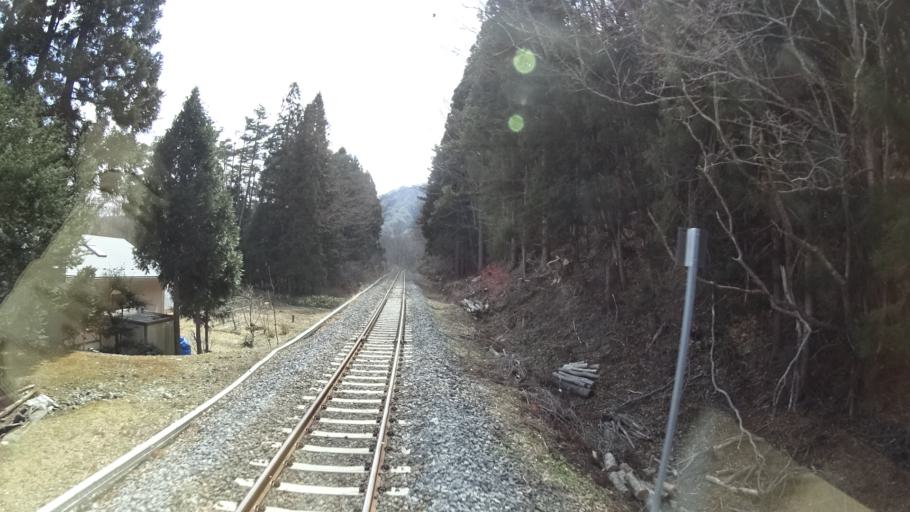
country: JP
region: Iwate
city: Yamada
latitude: 39.5172
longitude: 141.9156
